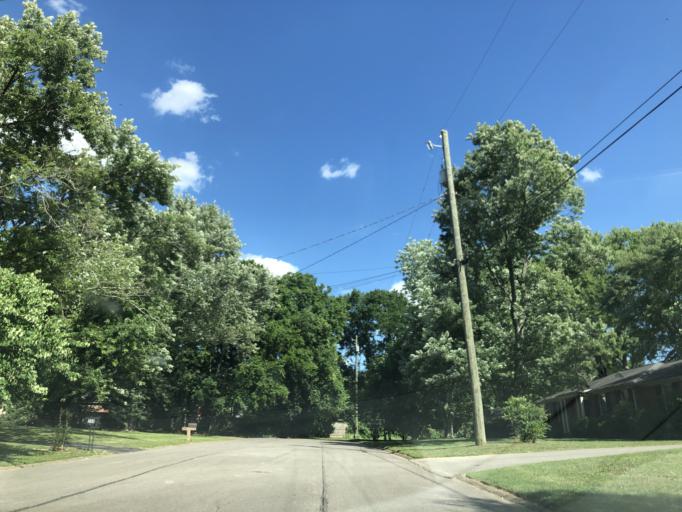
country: US
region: Tennessee
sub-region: Davidson County
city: Belle Meade
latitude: 36.0587
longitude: -86.9261
